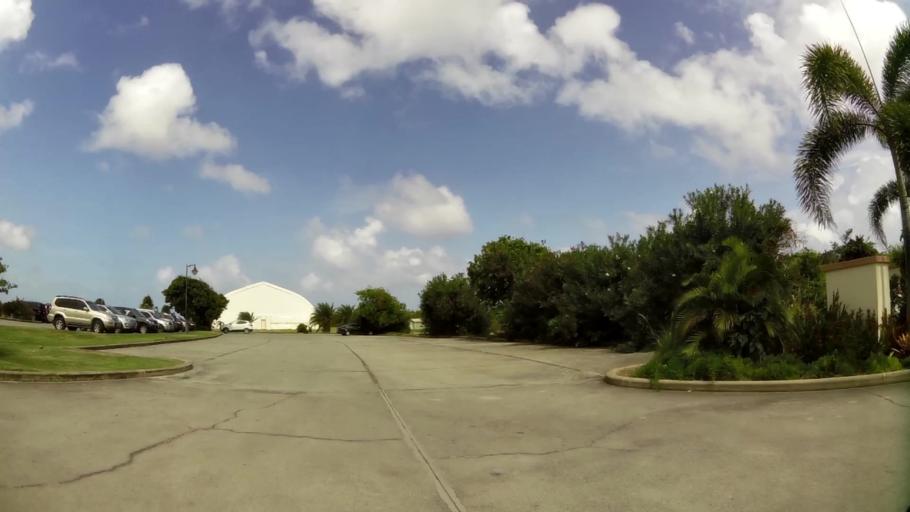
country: KN
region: Saint Peter Basseterre
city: Monkey Hill
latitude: 17.2965
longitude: -62.6868
